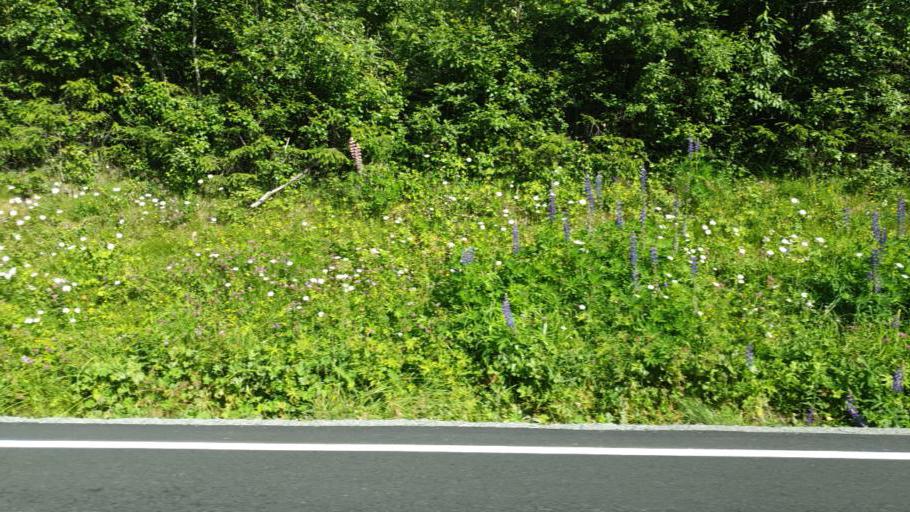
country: NO
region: Oppland
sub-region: Oystre Slidre
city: Heggenes
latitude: 61.1734
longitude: 8.9943
